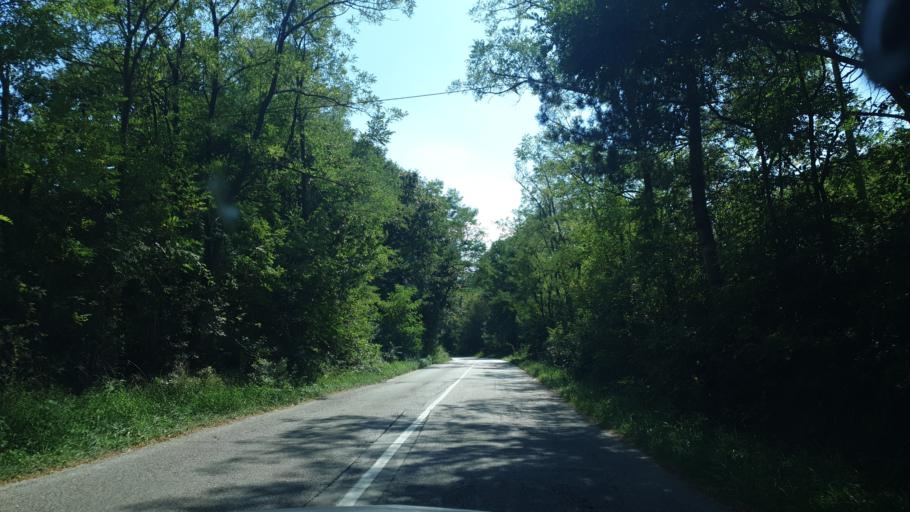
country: RS
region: Central Serbia
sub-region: Zlatiborski Okrug
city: Kosjeric
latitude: 44.0643
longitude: 20.0218
